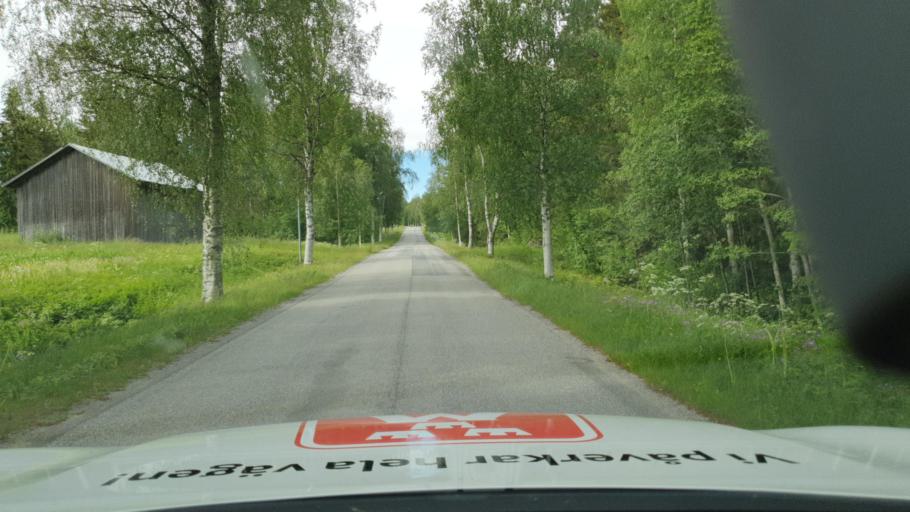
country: SE
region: Vaesterbotten
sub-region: Skelleftea Kommun
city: Burtraesk
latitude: 64.4316
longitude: 20.5176
